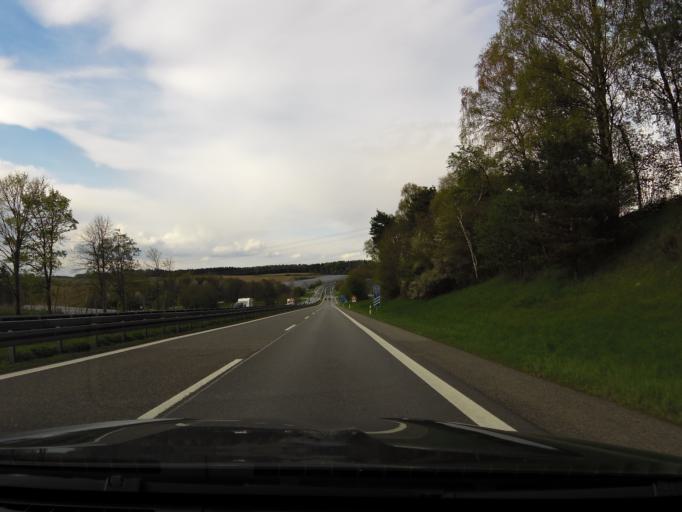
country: DE
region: Bavaria
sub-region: Upper Bavaria
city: Rudelzhausen
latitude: 48.6247
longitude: 11.7019
